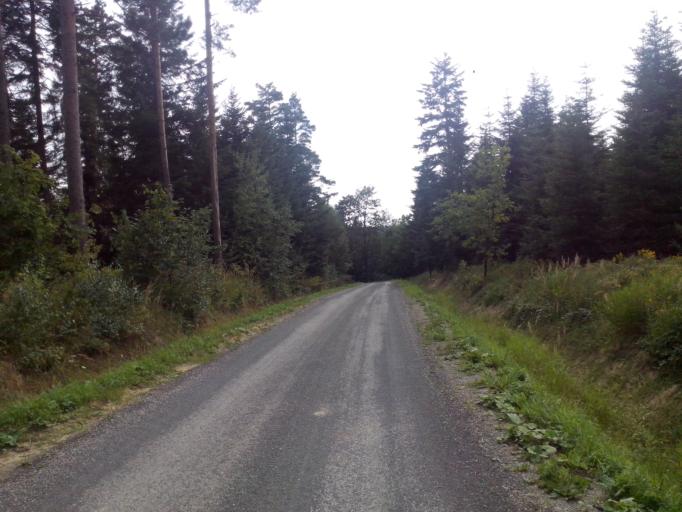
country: PL
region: Subcarpathian Voivodeship
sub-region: Powiat strzyzowski
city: Wysoka Strzyzowska
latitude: 49.8141
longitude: 21.7881
